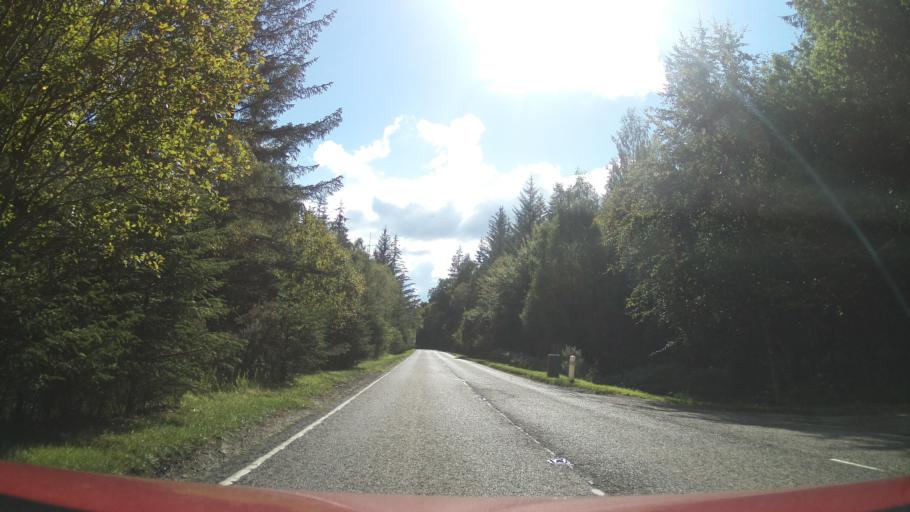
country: GB
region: Scotland
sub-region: Highland
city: Spean Bridge
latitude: 57.0771
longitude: -4.7656
